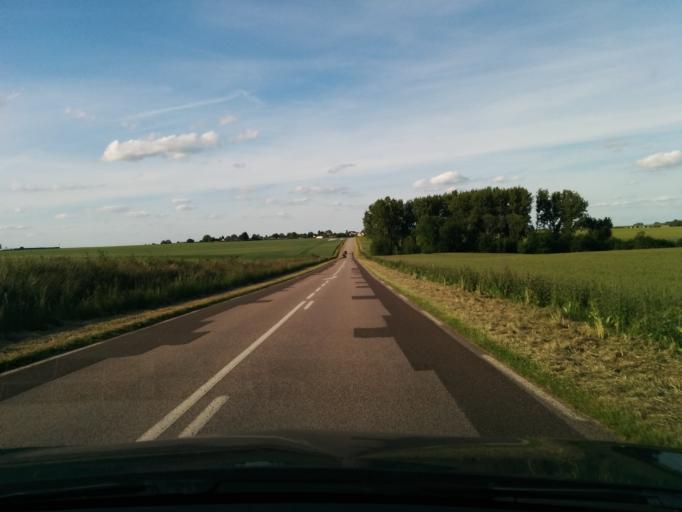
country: FR
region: Haute-Normandie
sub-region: Departement de l'Eure
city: Les Andelys
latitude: 49.2982
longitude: 1.4232
